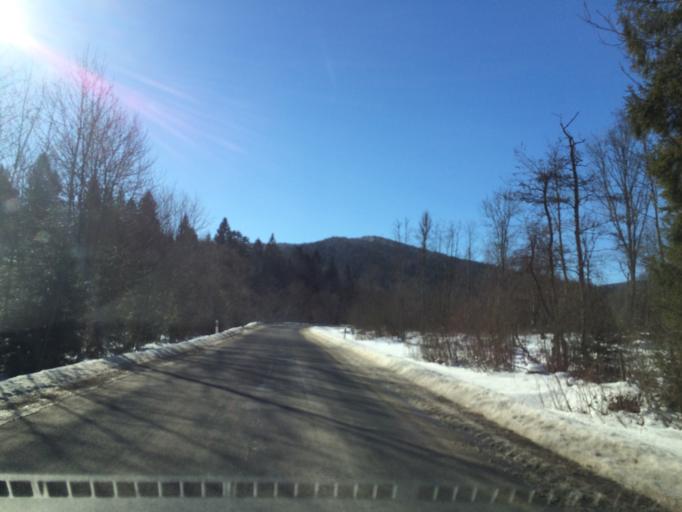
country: PL
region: Subcarpathian Voivodeship
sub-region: Powiat bieszczadzki
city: Lutowiska
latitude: 49.1545
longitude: 22.6863
